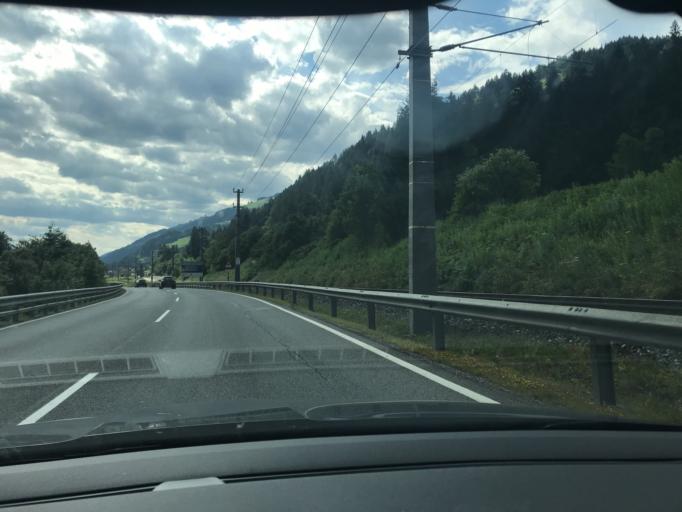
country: AT
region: Tyrol
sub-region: Politischer Bezirk Lienz
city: Leisach
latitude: 46.7856
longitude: 12.6828
